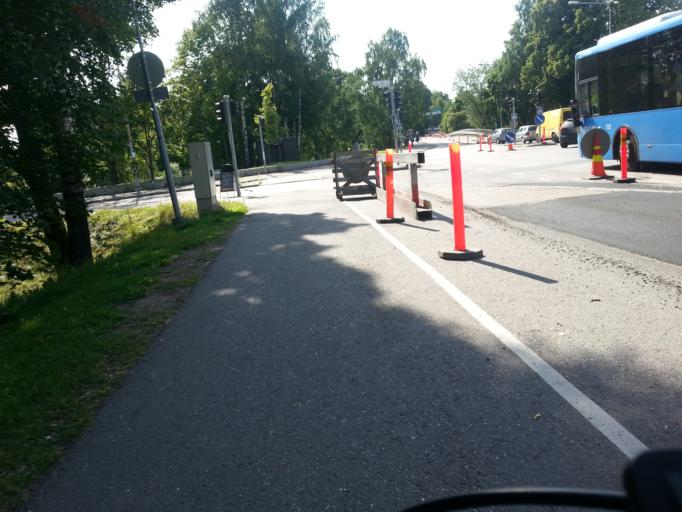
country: FI
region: Uusimaa
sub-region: Helsinki
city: Helsinki
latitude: 60.2176
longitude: 24.9835
